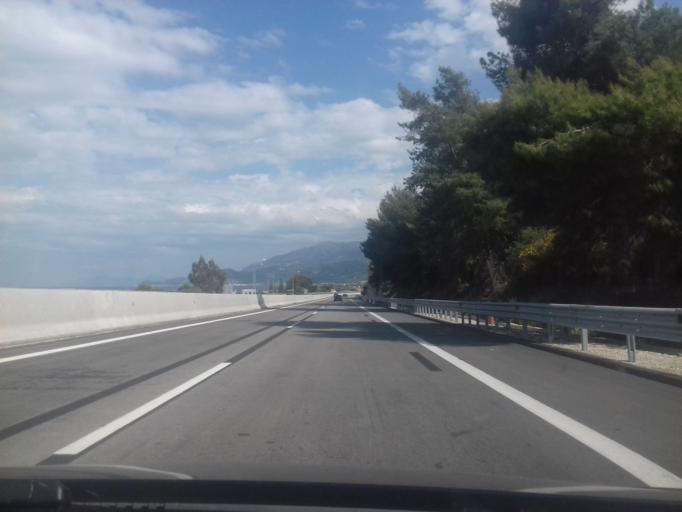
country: GR
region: West Greece
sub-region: Nomos Achaias
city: Siliveniotika
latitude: 38.1670
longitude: 22.3292
